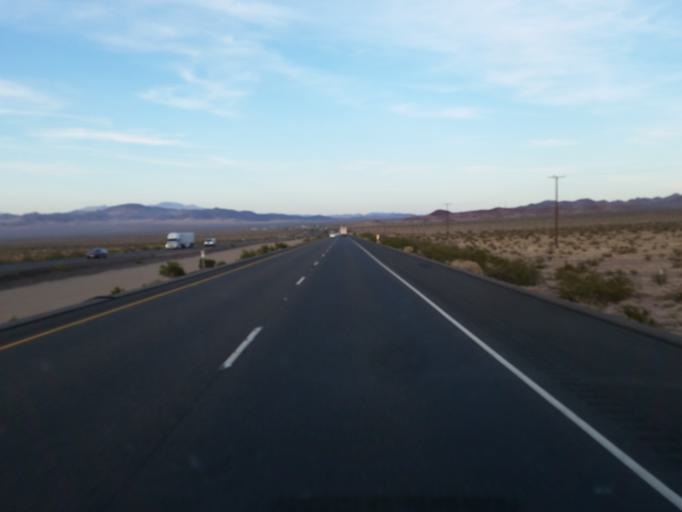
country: US
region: California
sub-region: San Bernardino County
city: Joshua Tree
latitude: 34.7247
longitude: -116.2143
